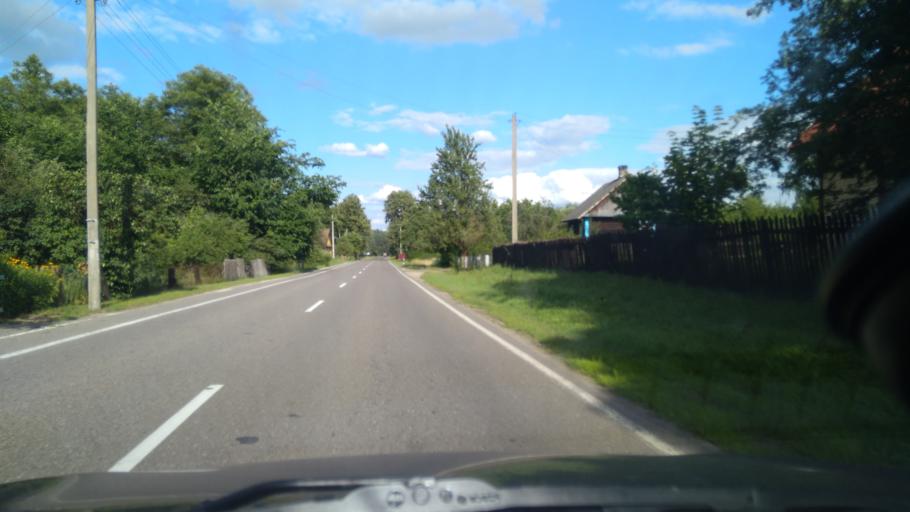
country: BY
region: Grodnenskaya
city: Masty
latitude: 53.3491
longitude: 24.6417
